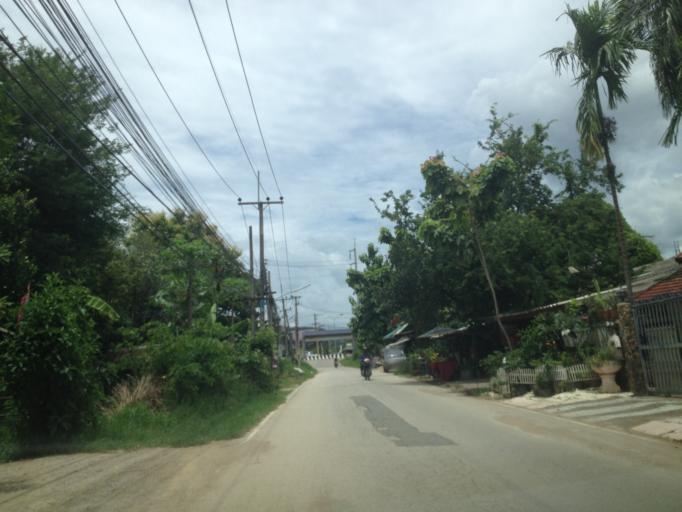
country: TH
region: Chiang Mai
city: Hang Dong
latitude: 18.7231
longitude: 98.9287
